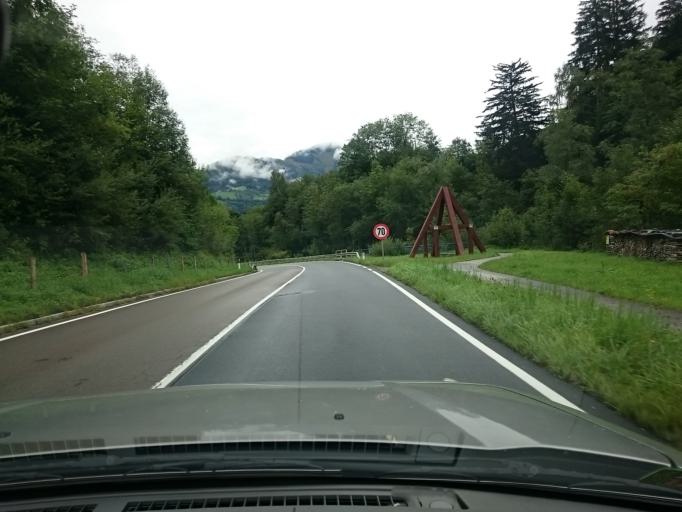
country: AT
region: Salzburg
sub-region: Politischer Bezirk Zell am See
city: Bruck an der Grossglocknerstrasse
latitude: 47.2642
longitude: 12.8243
